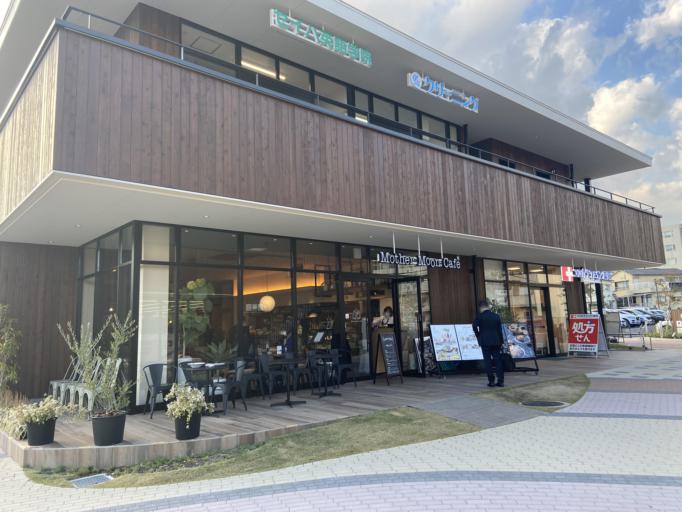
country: JP
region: Hyogo
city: Ashiya
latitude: 34.7391
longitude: 135.3194
